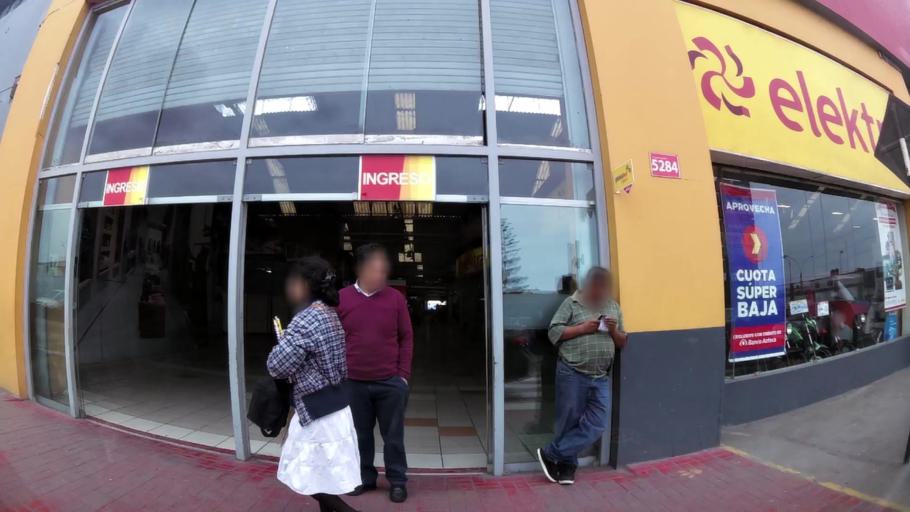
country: PE
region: Callao
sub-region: Callao
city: Callao
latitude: -12.0491
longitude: -77.1117
